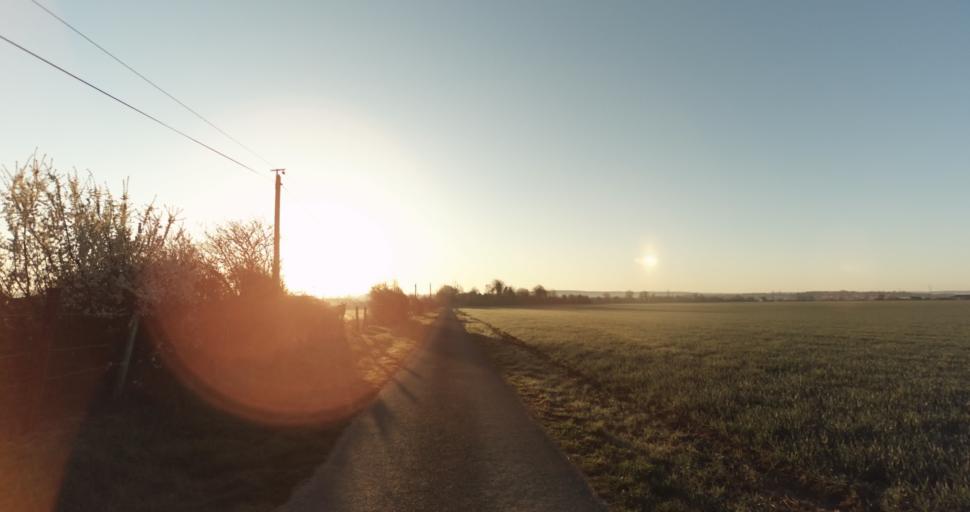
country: FR
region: Lower Normandy
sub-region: Departement du Calvados
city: Saint-Pierre-sur-Dives
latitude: 49.0380
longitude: -0.0393
